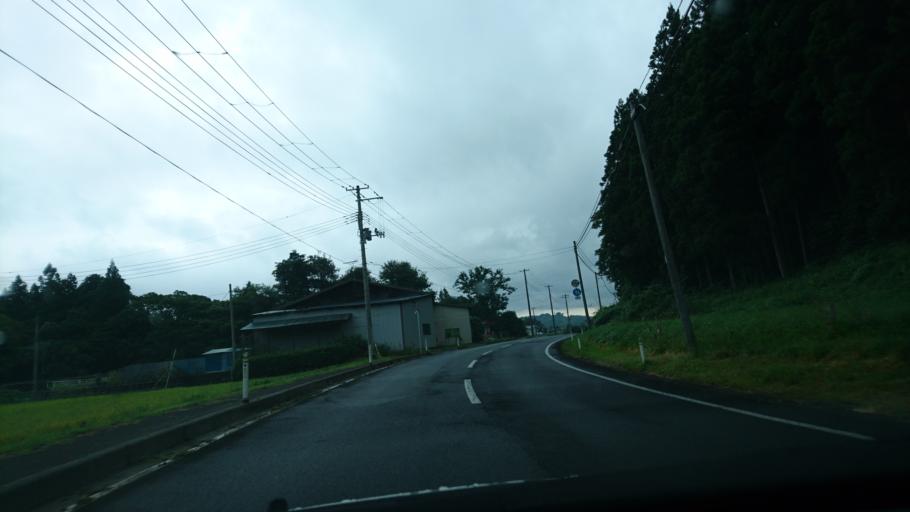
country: JP
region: Iwate
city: Ichinoseki
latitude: 38.9179
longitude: 141.0864
